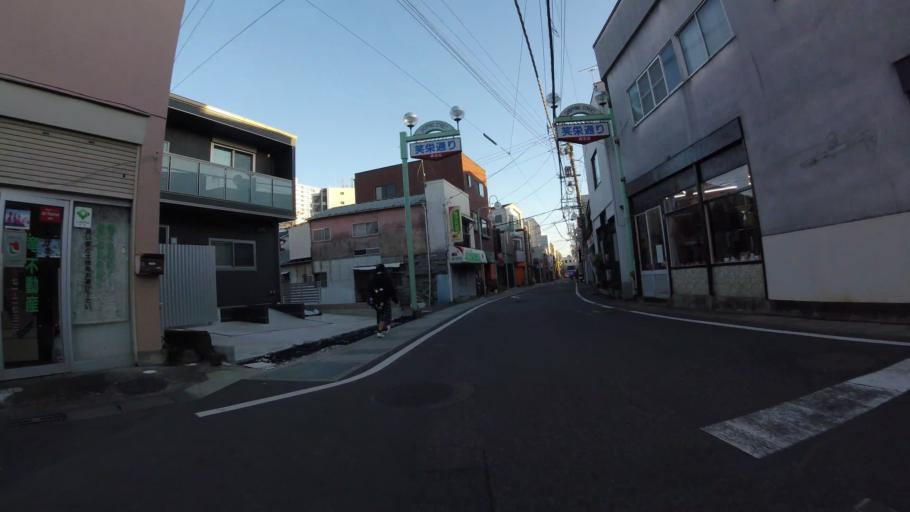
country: JP
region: Shizuoka
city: Mishima
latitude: 35.1208
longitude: 138.9105
